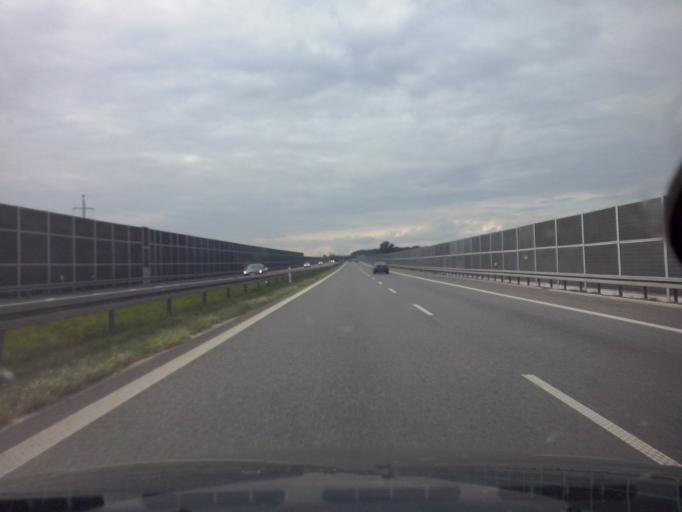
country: PL
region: Lesser Poland Voivodeship
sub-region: Powiat bochenski
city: Bochnia
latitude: 50.0038
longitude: 20.4382
